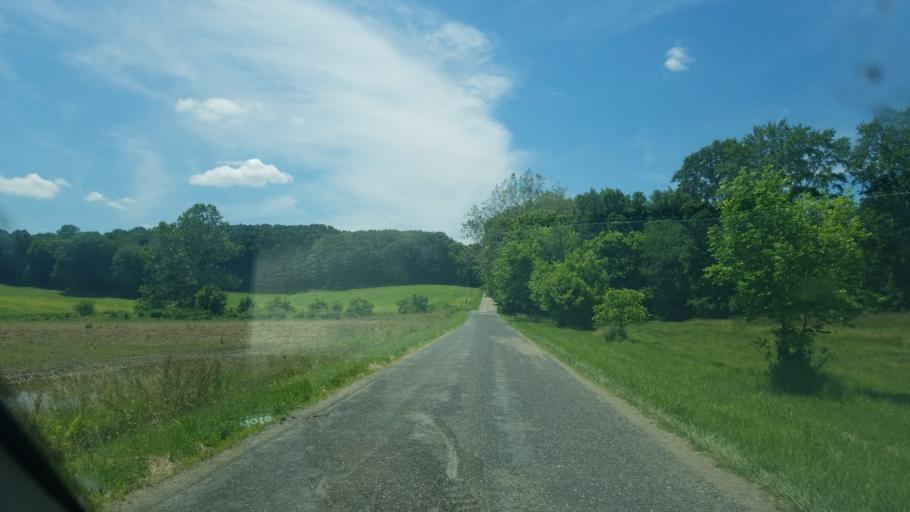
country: US
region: Ohio
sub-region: Mahoning County
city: Sebring
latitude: 40.8577
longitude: -80.9963
